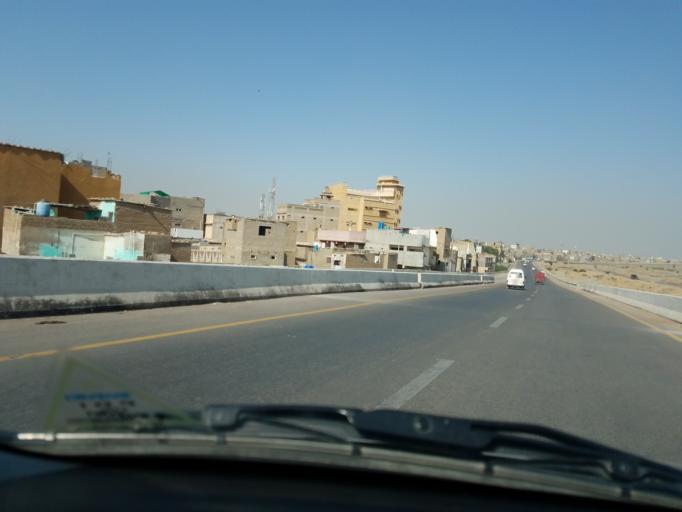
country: PK
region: Sindh
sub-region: Karachi District
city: Karachi
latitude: 24.8854
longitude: 67.0222
